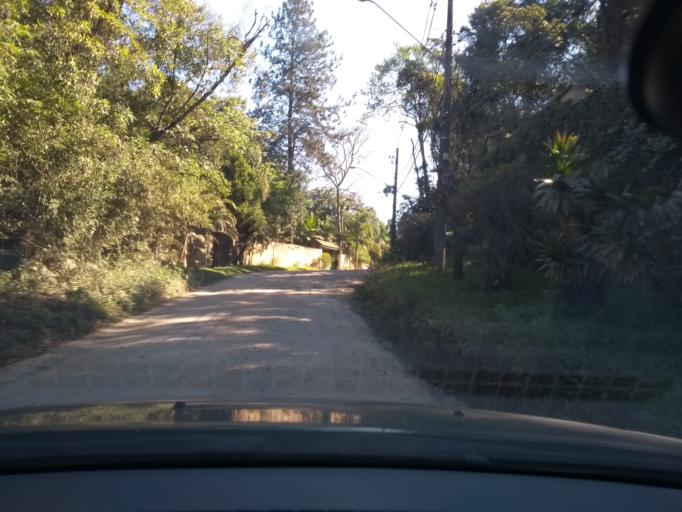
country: BR
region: Sao Paulo
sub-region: Rio Grande Da Serra
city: Rio Grande da Serra
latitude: -23.7625
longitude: -46.4707
